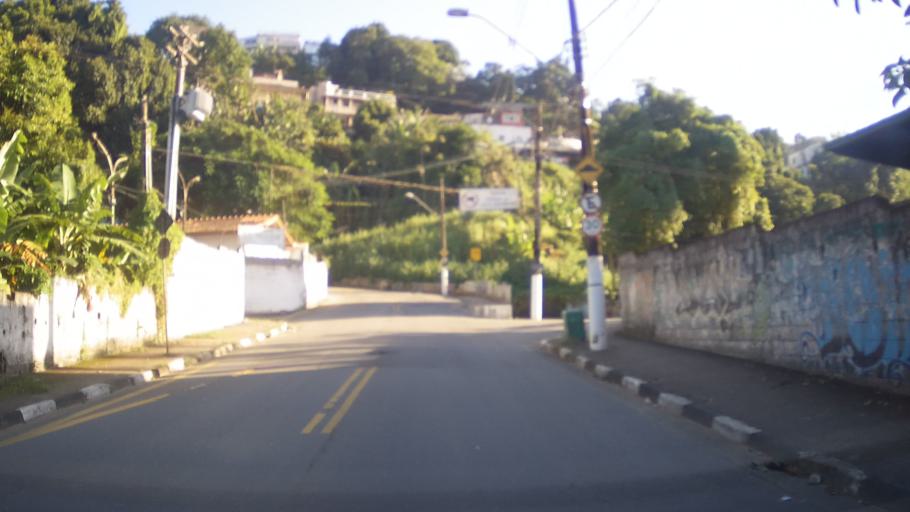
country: BR
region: Sao Paulo
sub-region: Santos
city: Santos
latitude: -23.9410
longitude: -46.3374
